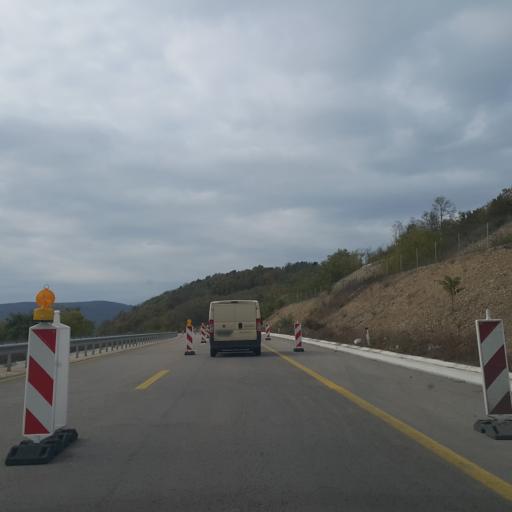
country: RS
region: Central Serbia
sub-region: Pirotski Okrug
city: Bela Palanka
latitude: 43.2362
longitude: 22.3059
